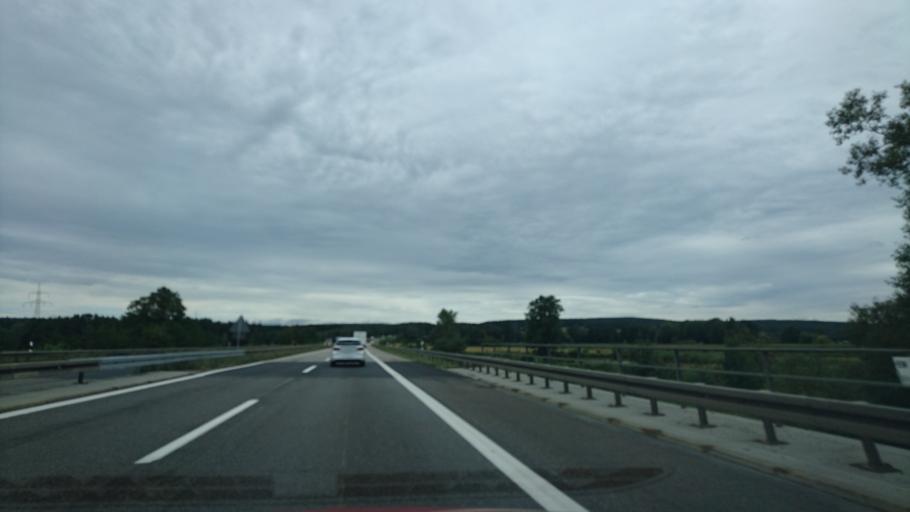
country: DE
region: Bavaria
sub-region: Upper Palatinate
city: Wernberg-Koblitz
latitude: 49.5498
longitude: 12.1264
